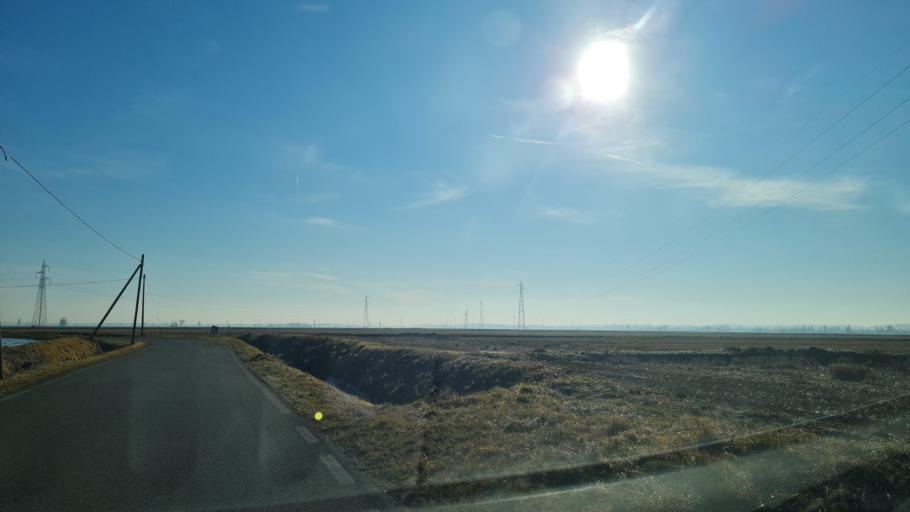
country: IT
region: Piedmont
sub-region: Provincia di Biella
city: Villanova Biellese
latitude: 45.4507
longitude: 8.1698
